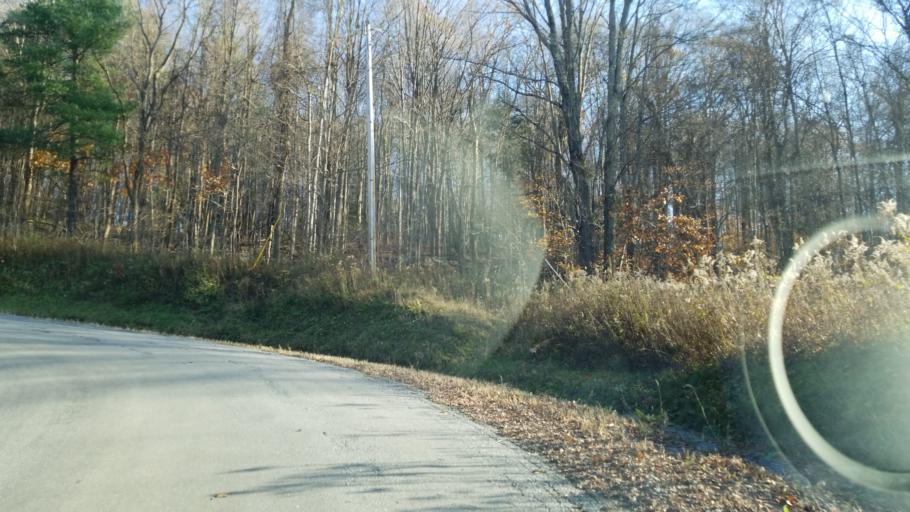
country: US
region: Pennsylvania
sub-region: Clearfield County
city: Treasure Lake
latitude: 41.1519
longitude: -78.6648
